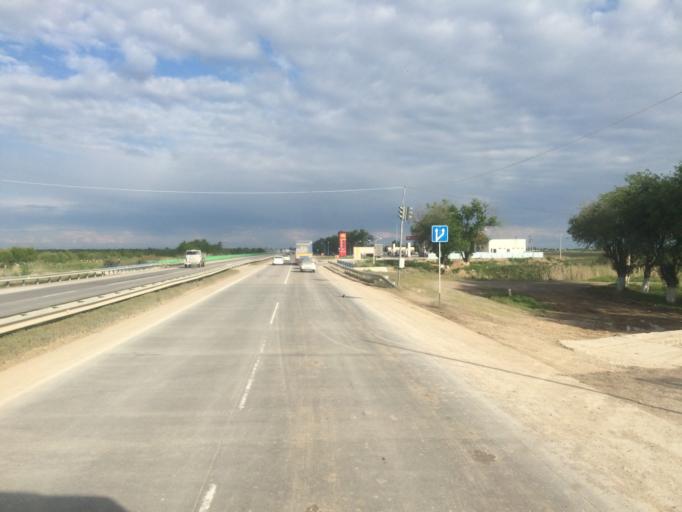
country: KZ
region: Ongtustik Qazaqstan
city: Turkestan
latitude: 43.2706
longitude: 68.3487
